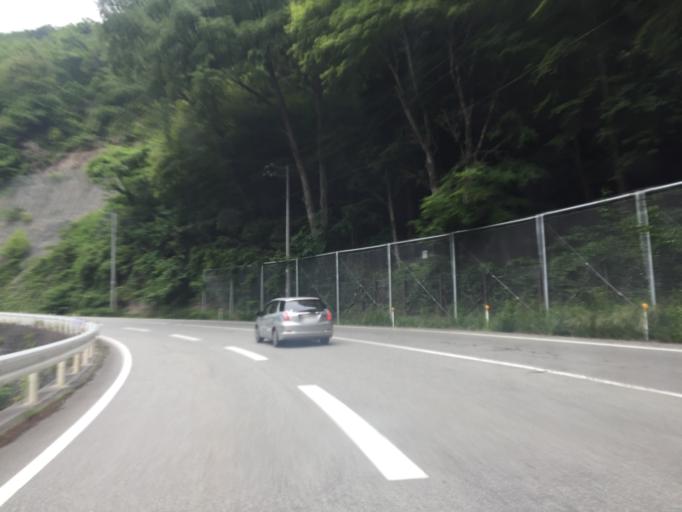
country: JP
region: Fukushima
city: Namie
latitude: 37.4194
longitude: 140.8990
